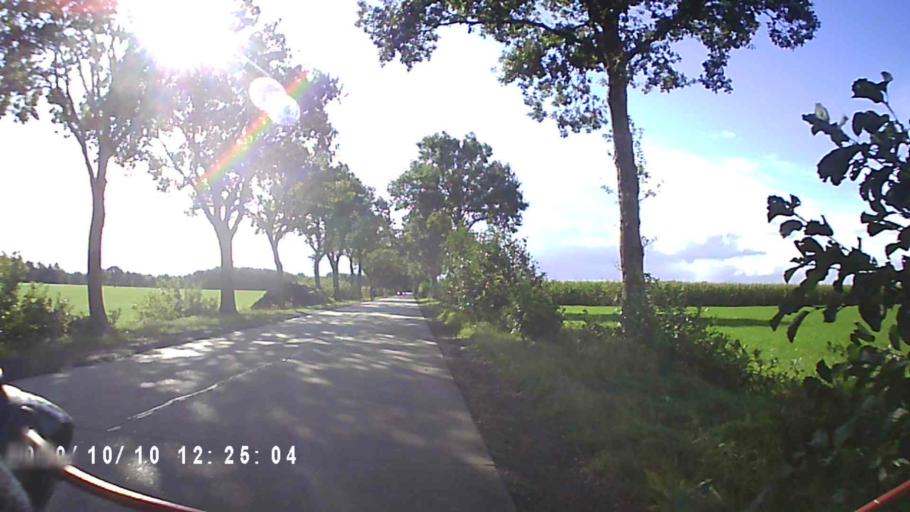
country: NL
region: Friesland
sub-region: Gemeente Heerenveen
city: Jubbega
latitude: 52.9905
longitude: 6.1800
